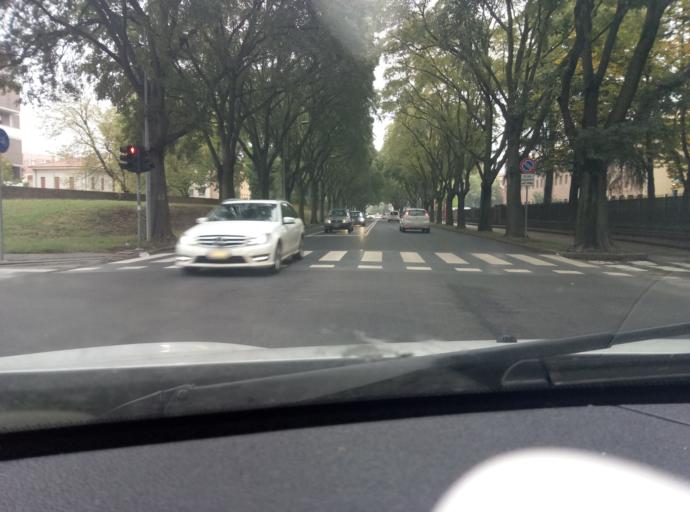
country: IT
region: Emilia-Romagna
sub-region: Provincia di Ferrara
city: Ferrara
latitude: 44.8414
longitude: 11.6067
